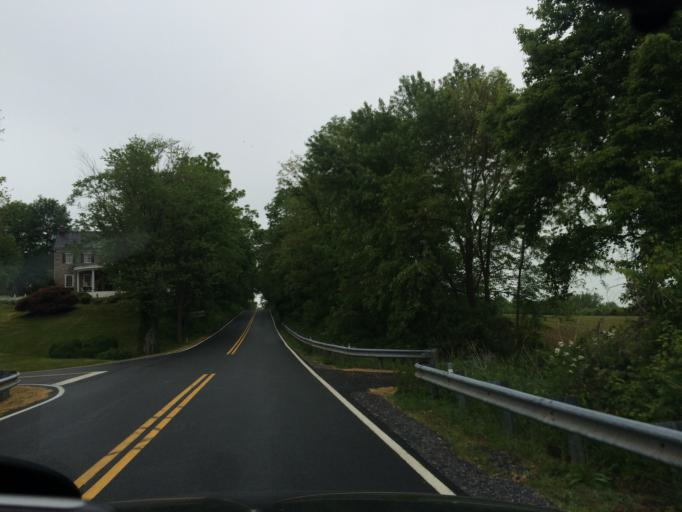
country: US
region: Maryland
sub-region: Frederick County
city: Woodsboro
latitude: 39.6037
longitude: -77.2706
